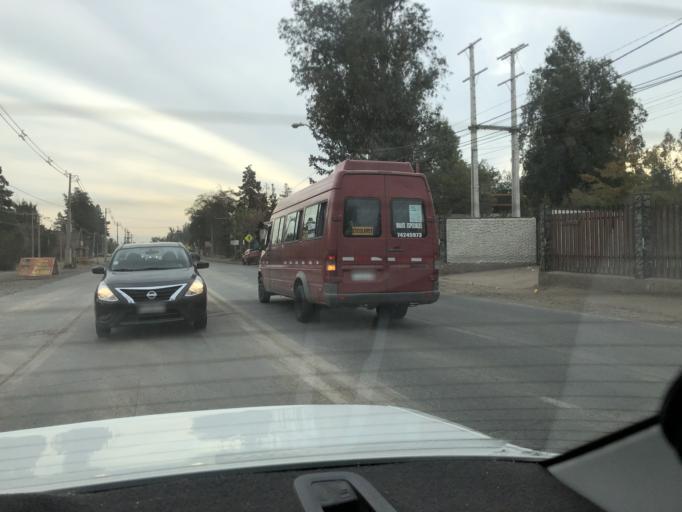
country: CL
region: Santiago Metropolitan
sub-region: Provincia de Cordillera
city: Puente Alto
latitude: -33.5982
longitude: -70.5215
